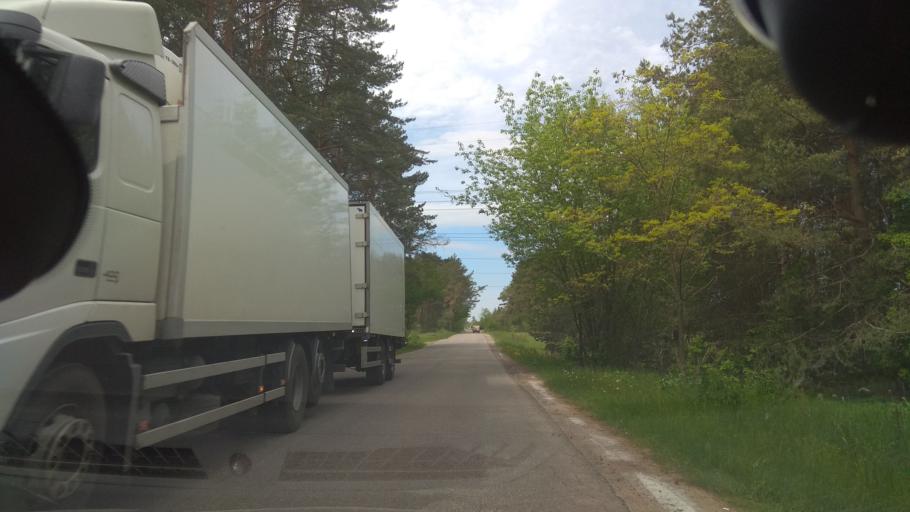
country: LT
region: Kauno apskritis
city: Jonava
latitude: 55.0882
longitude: 24.2946
